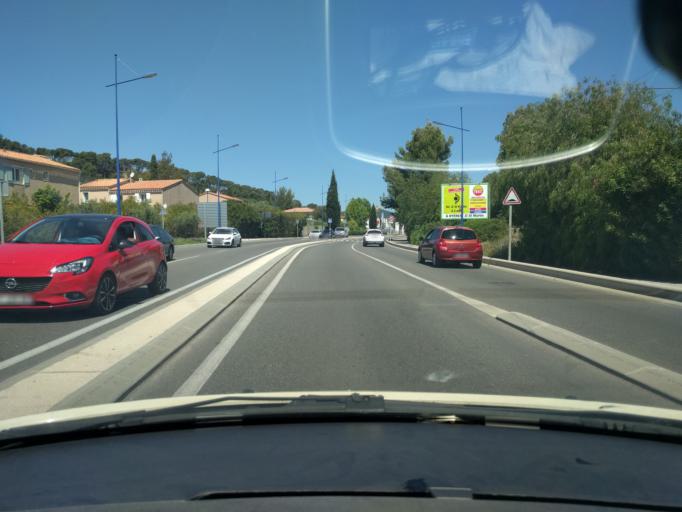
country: FR
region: Provence-Alpes-Cote d'Azur
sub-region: Departement du Var
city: Hyeres
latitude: 43.1020
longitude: 6.1299
